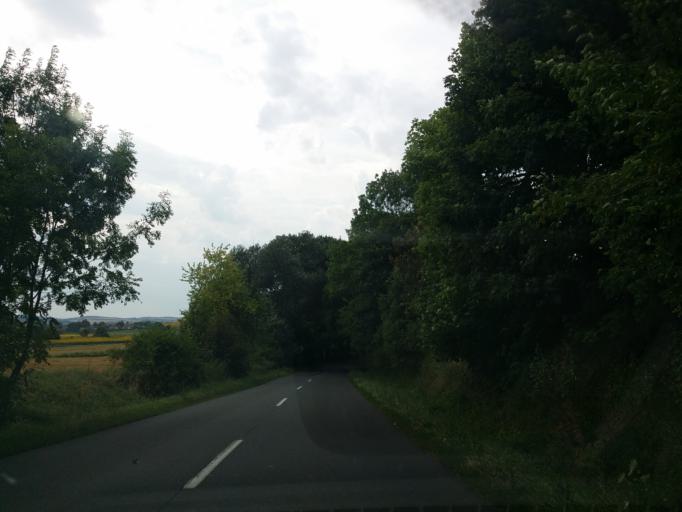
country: HU
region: Nograd
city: Bercel
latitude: 47.9766
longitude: 19.3999
